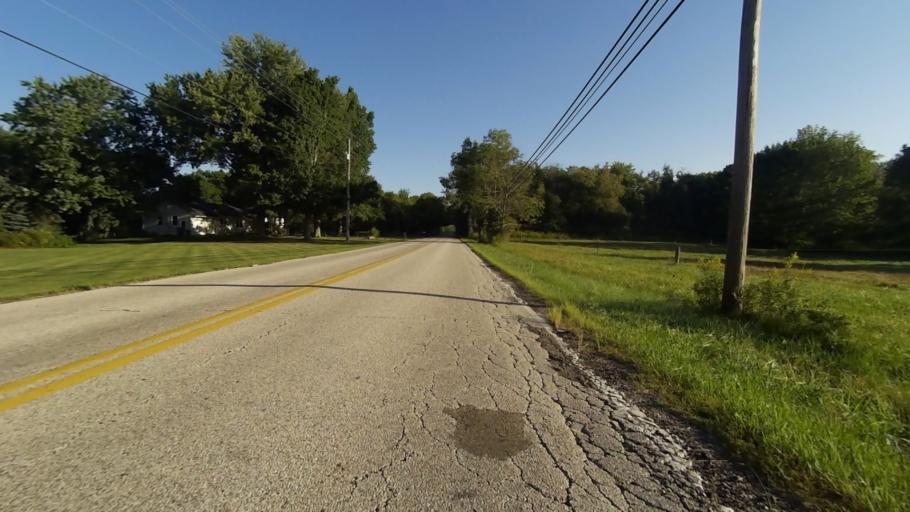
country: US
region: Ohio
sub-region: Portage County
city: Kent
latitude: 41.1761
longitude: -81.3657
